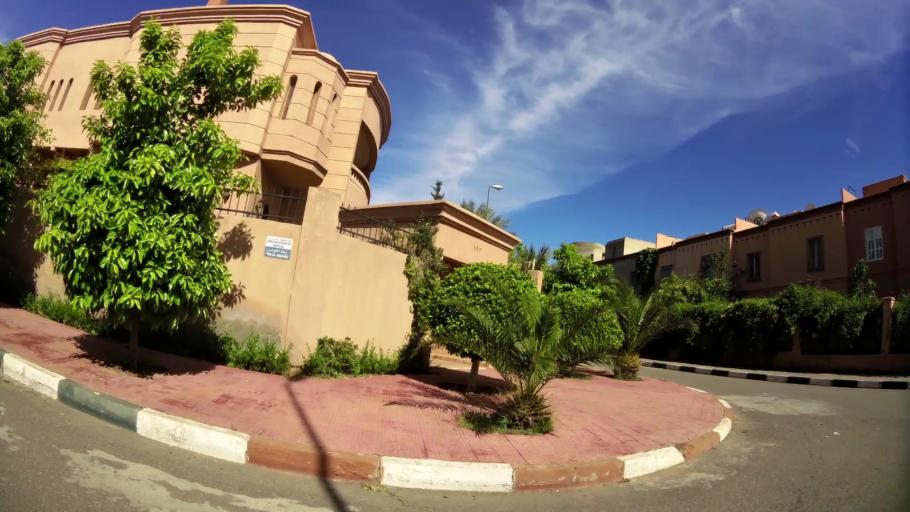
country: MA
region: Marrakech-Tensift-Al Haouz
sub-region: Marrakech
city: Marrakesh
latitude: 31.6533
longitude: -8.0548
